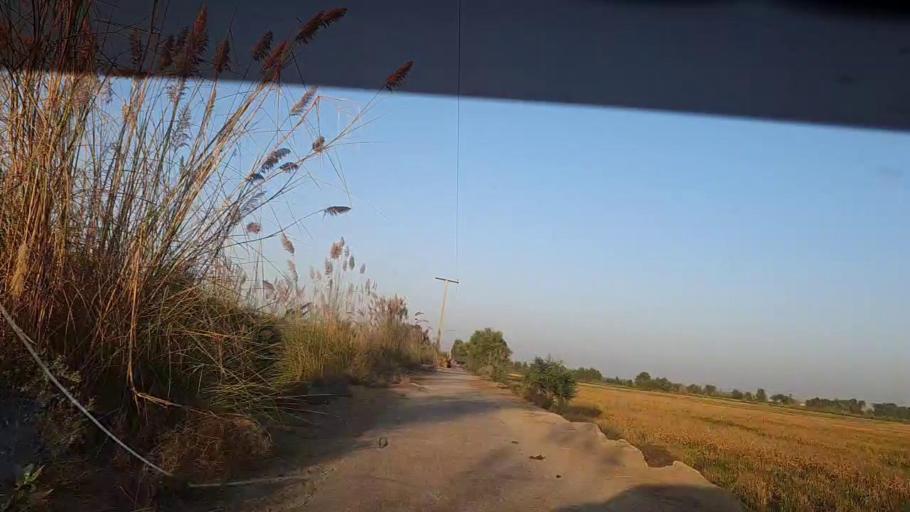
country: PK
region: Sindh
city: Ratodero
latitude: 27.8901
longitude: 68.2189
